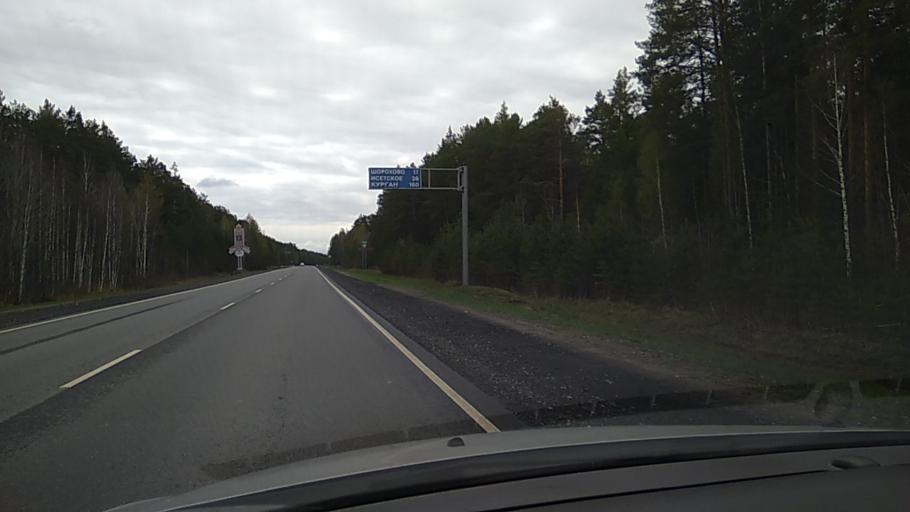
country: RU
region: Tjumen
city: Chervishevo
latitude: 56.8194
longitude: 65.3798
